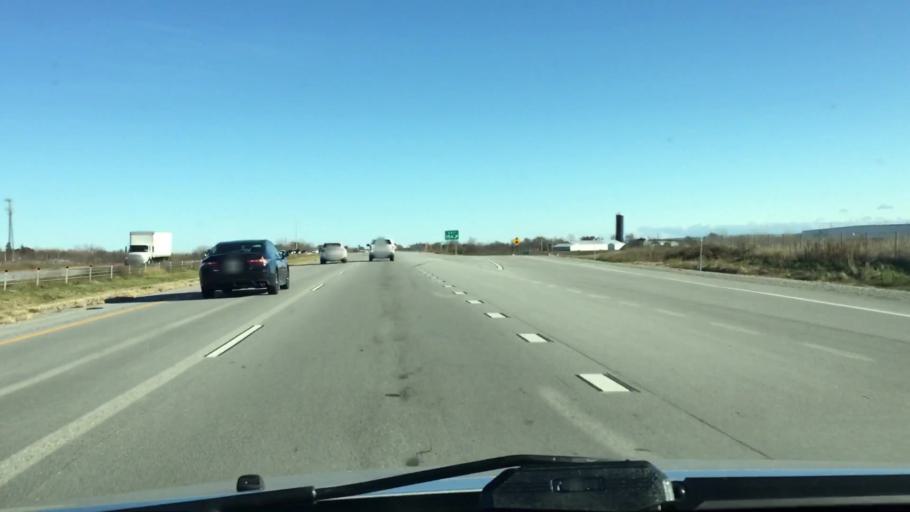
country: US
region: Wisconsin
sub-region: Brown County
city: Wrightstown
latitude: 44.3462
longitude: -88.1959
